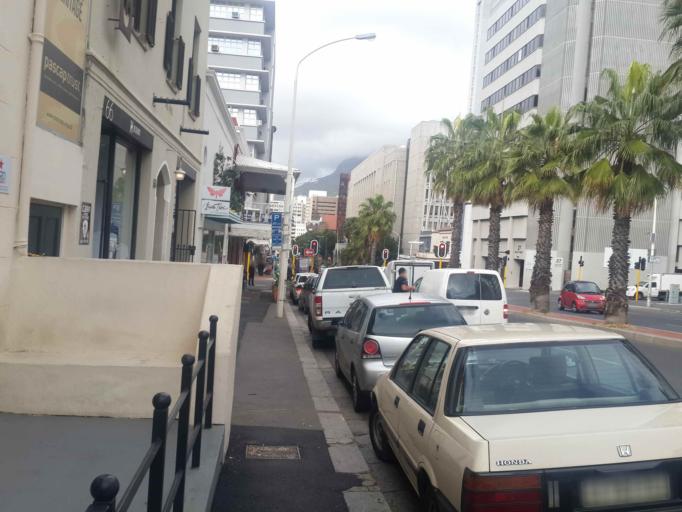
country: ZA
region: Western Cape
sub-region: City of Cape Town
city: Cape Town
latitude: -33.9228
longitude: 18.4169
